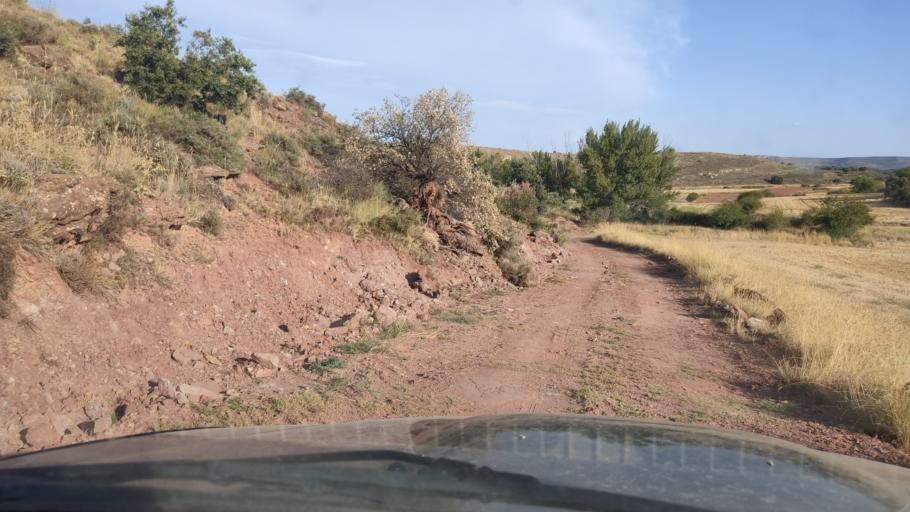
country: ES
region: Aragon
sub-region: Provincia de Teruel
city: Monforte de Moyuela
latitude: 41.0306
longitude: -1.0113
